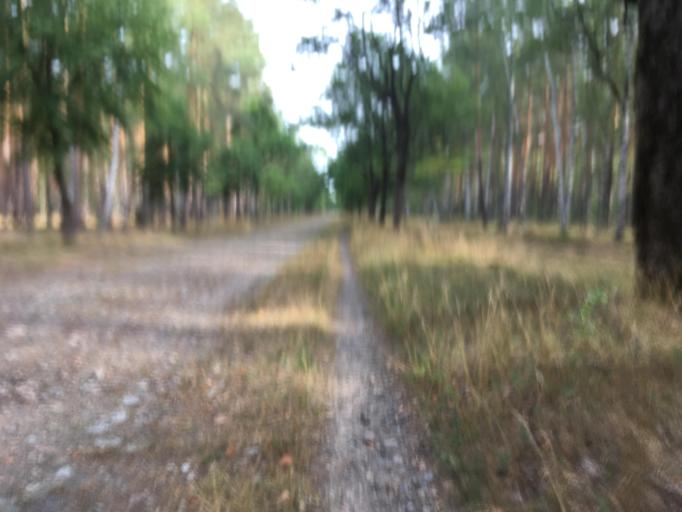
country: DE
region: Brandenburg
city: Marienwerder
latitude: 52.9335
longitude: 13.5196
